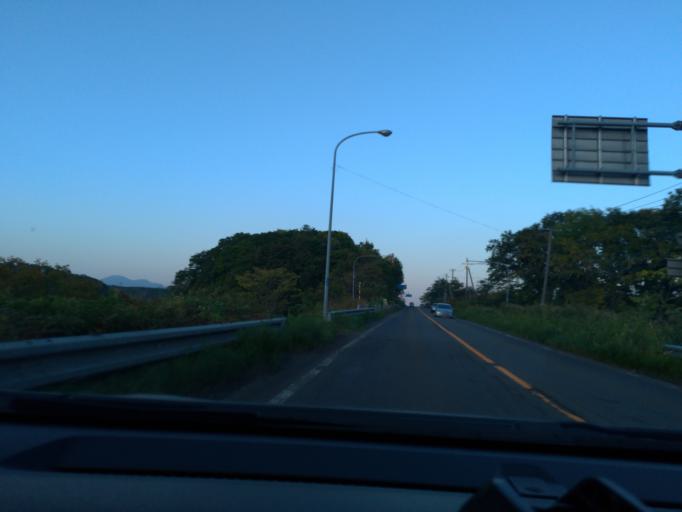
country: JP
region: Hokkaido
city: Tobetsu
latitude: 43.3161
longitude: 141.6016
